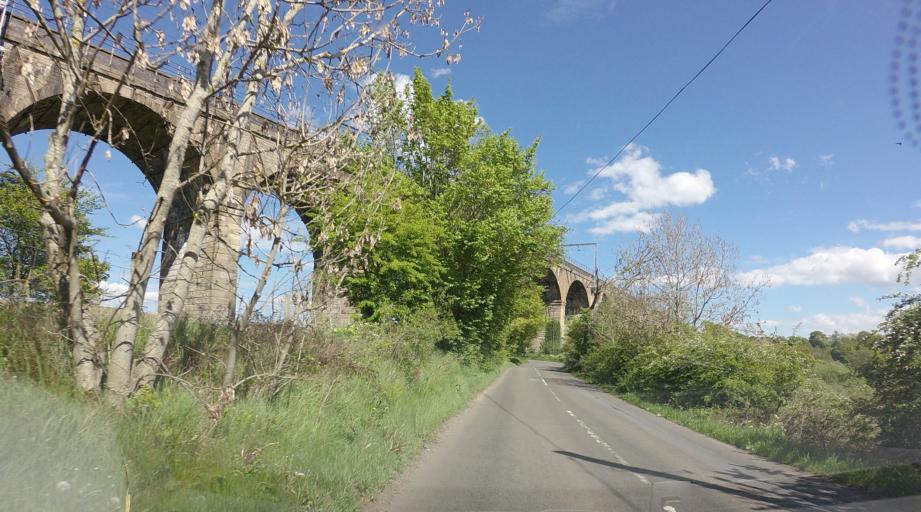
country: GB
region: Scotland
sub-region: West Lothian
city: Linlithgow
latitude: 55.9747
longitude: -3.6362
